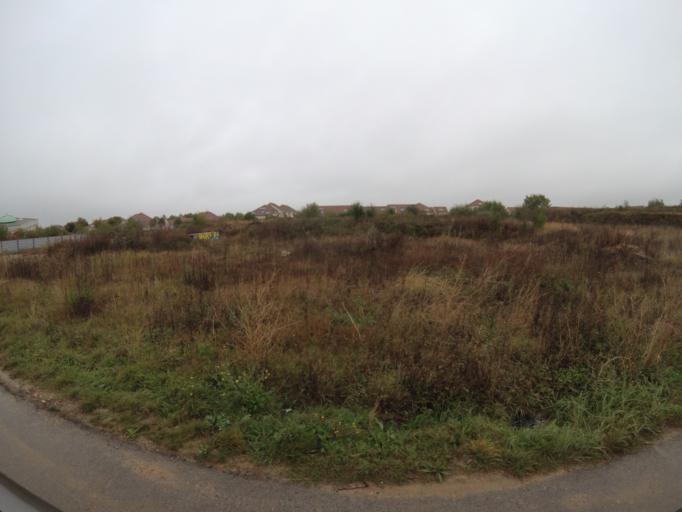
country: FR
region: Ile-de-France
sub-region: Departement de Seine-et-Marne
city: Chanteloup-en-Brie
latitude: 48.8382
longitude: 2.7305
